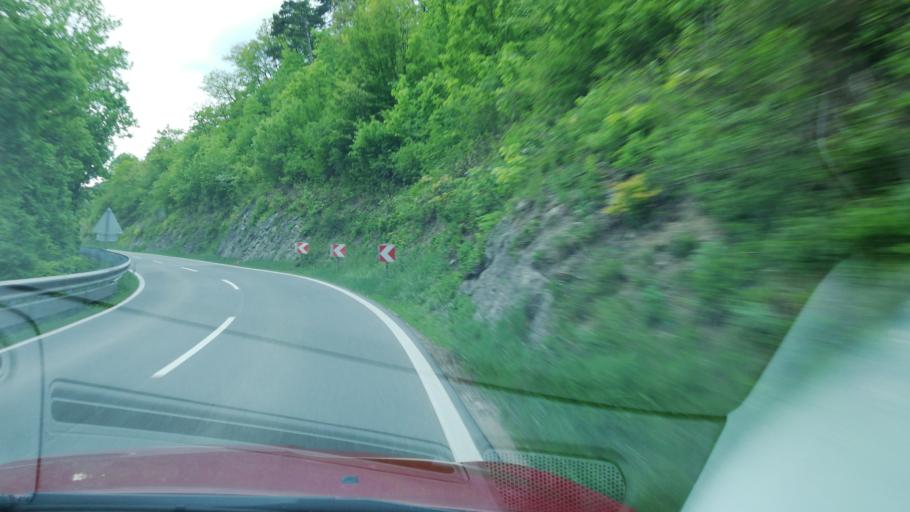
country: AT
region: Lower Austria
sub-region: Politischer Bezirk Baden
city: Heiligenkreuz
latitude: 48.0253
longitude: 16.1584
